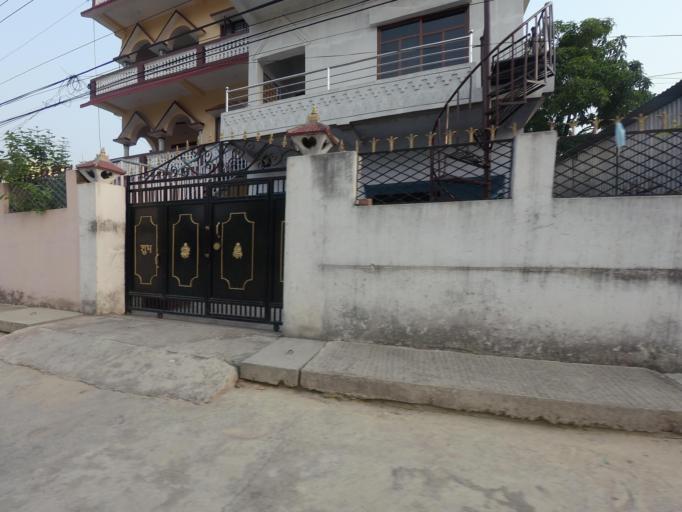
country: NP
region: Western Region
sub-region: Lumbini Zone
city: Bhairahawa
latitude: 27.5143
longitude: 83.4589
